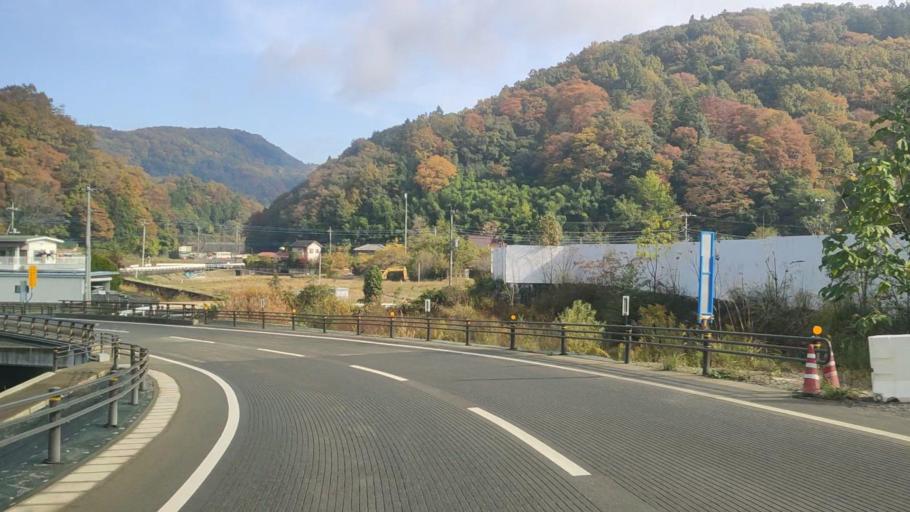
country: JP
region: Yamanashi
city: Ryuo
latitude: 35.4601
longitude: 138.4536
